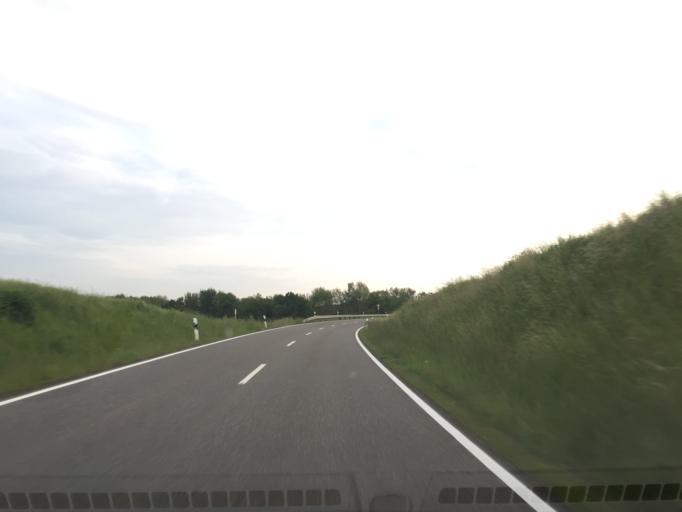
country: DE
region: Rheinland-Pfalz
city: Weroth
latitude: 50.4525
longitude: 7.9478
